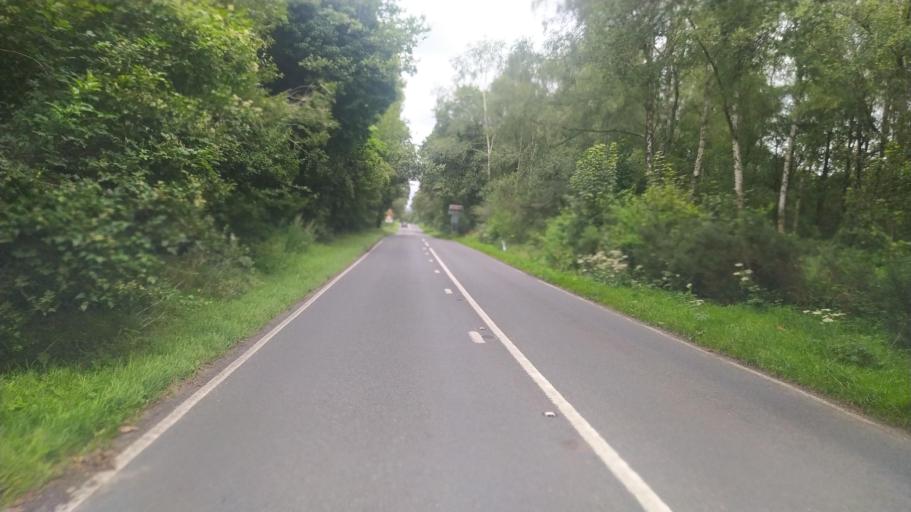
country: GB
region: England
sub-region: Hampshire
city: Liphook
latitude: 51.0574
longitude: -0.8153
